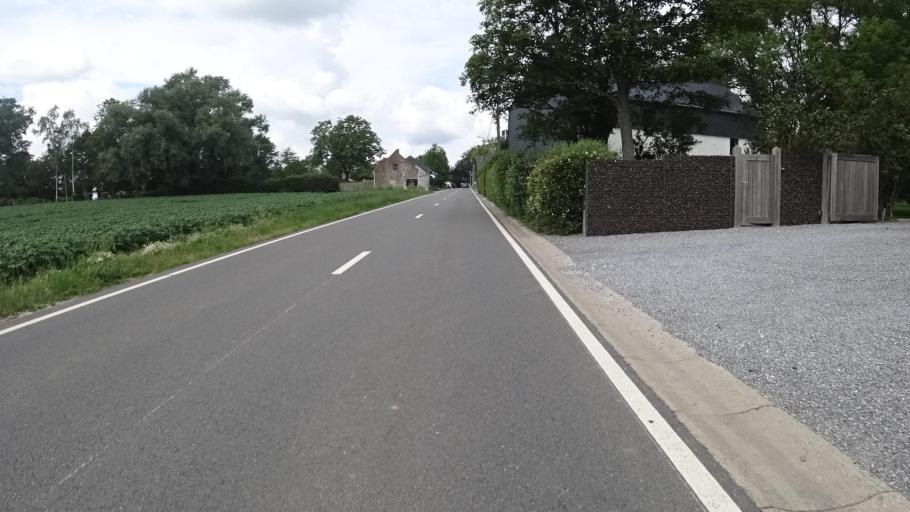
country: BE
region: Wallonia
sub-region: Province de Namur
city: Namur
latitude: 50.5406
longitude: 4.8414
